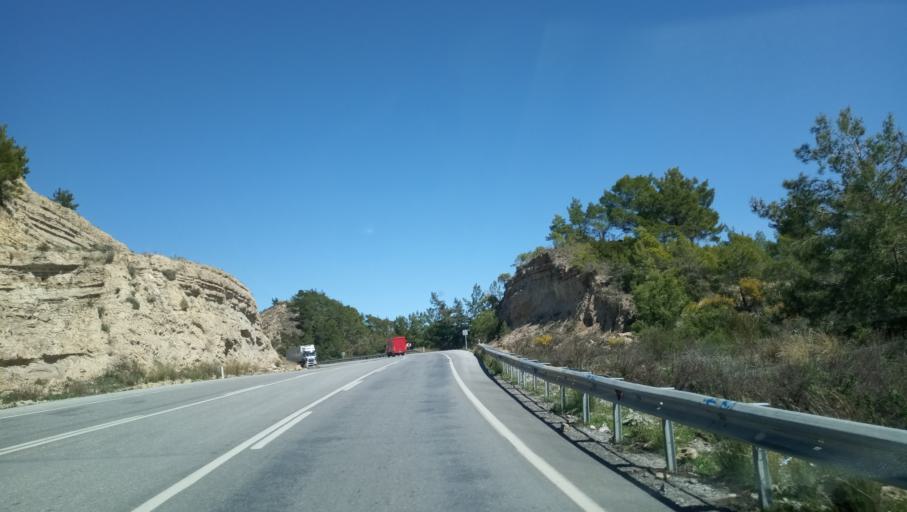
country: TR
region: Antalya
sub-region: Manavgat
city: Kizilagac
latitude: 36.7463
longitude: 31.6195
